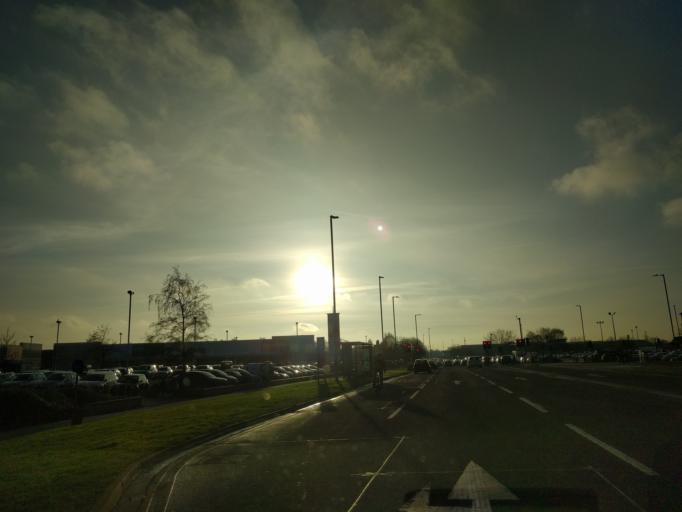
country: GB
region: England
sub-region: Lincolnshire
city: Lincoln
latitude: 53.2250
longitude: -0.5519
